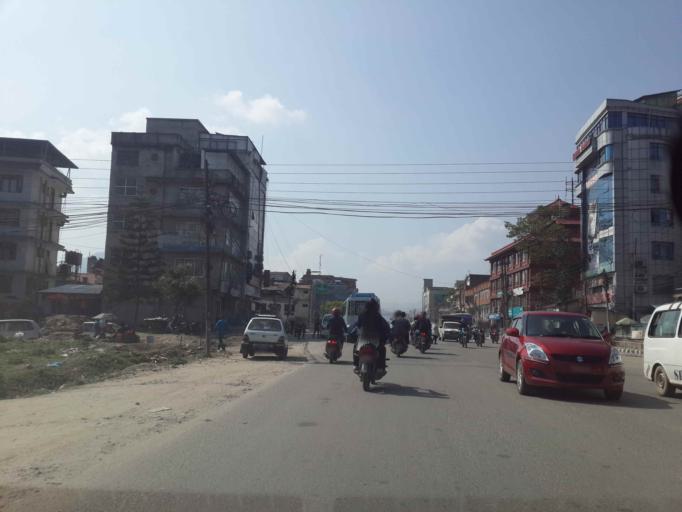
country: NP
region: Central Region
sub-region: Bagmati Zone
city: Kathmandu
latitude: 27.7392
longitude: 85.3387
